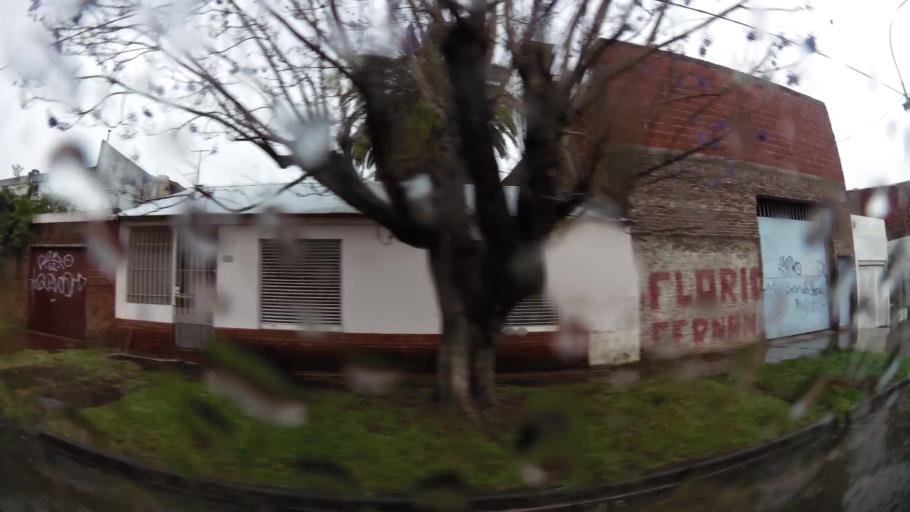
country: AR
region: Buenos Aires
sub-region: Partido de Lanus
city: Lanus
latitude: -34.7102
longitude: -58.4144
